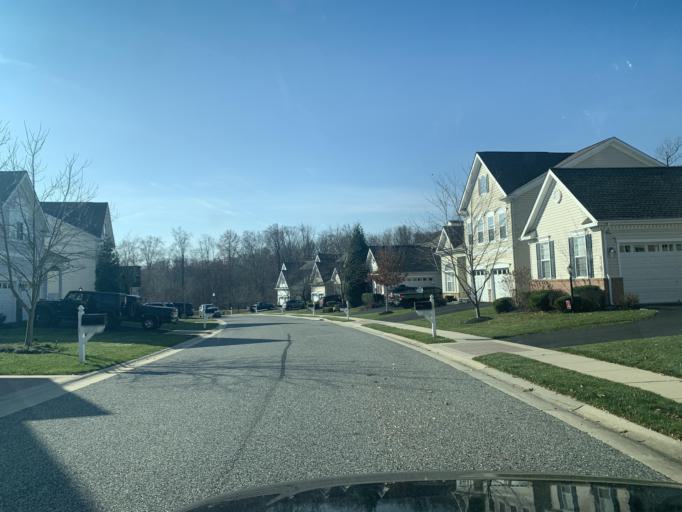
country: US
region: Maryland
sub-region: Harford County
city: Havre de Grace
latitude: 39.5453
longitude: -76.1235
